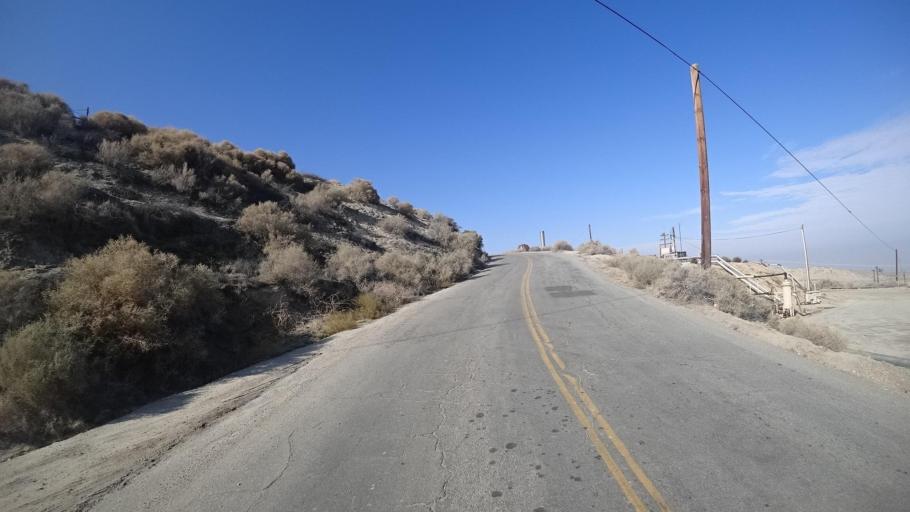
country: US
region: California
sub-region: Kern County
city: Taft Heights
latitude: 35.1208
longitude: -119.4748
